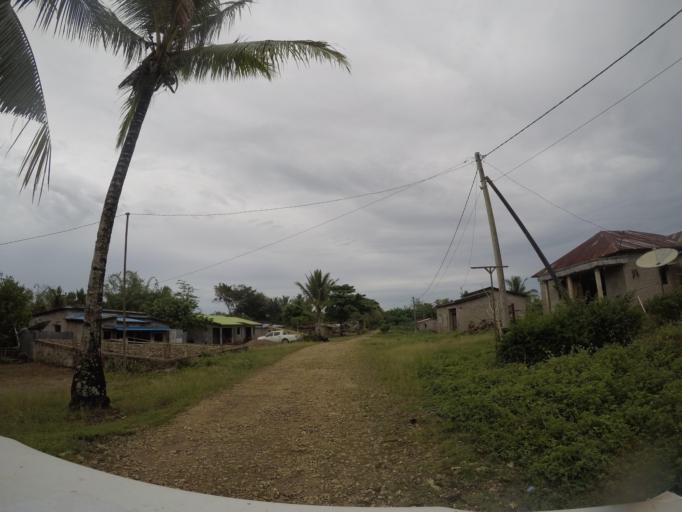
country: TL
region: Lautem
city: Lospalos
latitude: -8.5316
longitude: 127.0017
